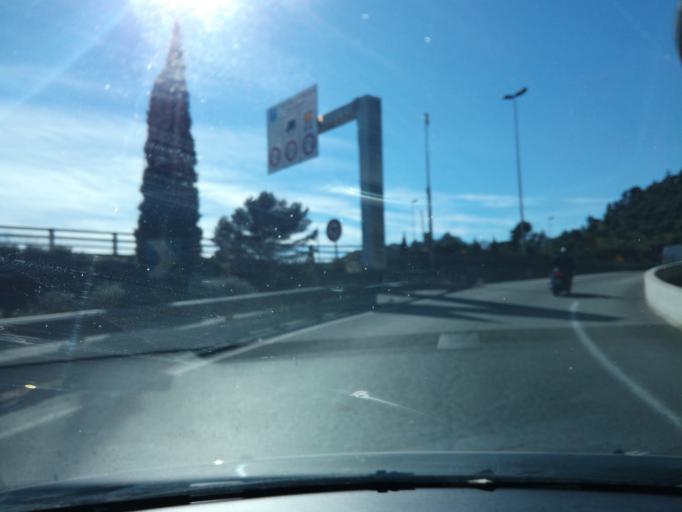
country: FR
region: Provence-Alpes-Cote d'Azur
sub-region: Departement des Alpes-Maritimes
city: Saint-Andre-de-la-Roche
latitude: 43.7338
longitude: 7.2889
